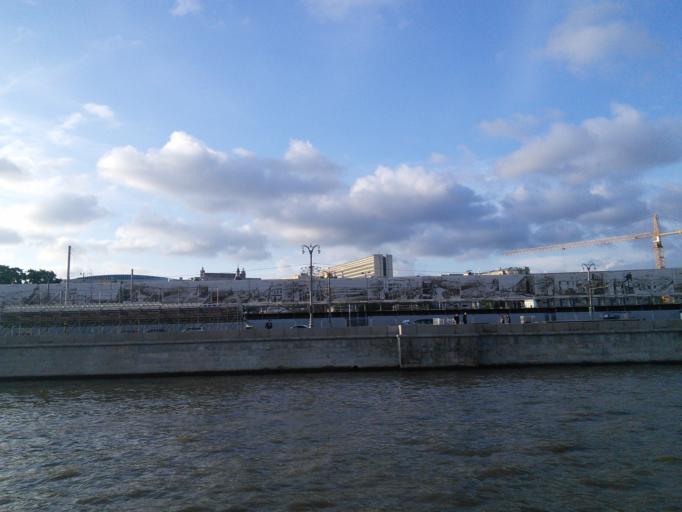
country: RU
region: Moscow
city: Moscow
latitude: 55.7492
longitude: 37.6282
